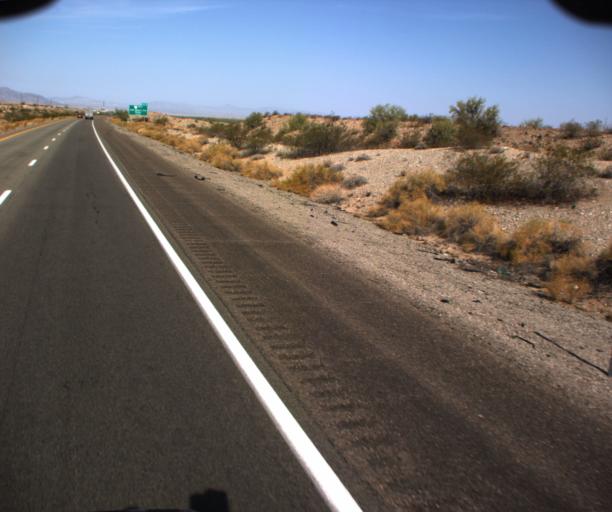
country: US
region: Arizona
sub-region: Mohave County
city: Desert Hills
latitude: 34.7311
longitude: -114.2764
